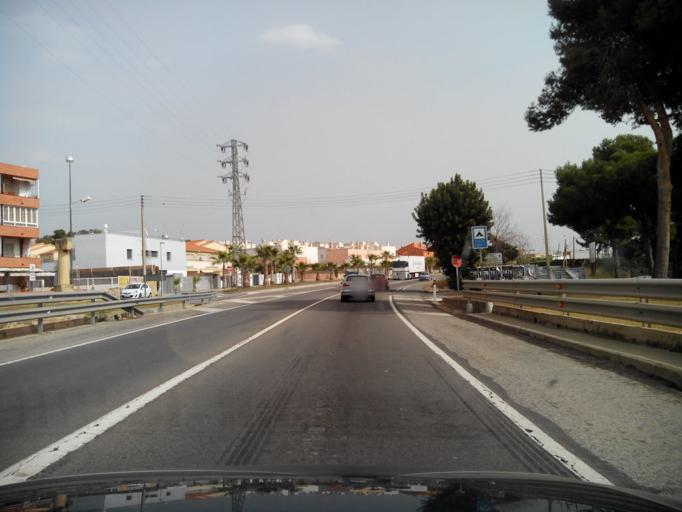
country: ES
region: Catalonia
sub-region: Provincia de Tarragona
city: Creixell
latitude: 41.1604
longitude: 1.4361
